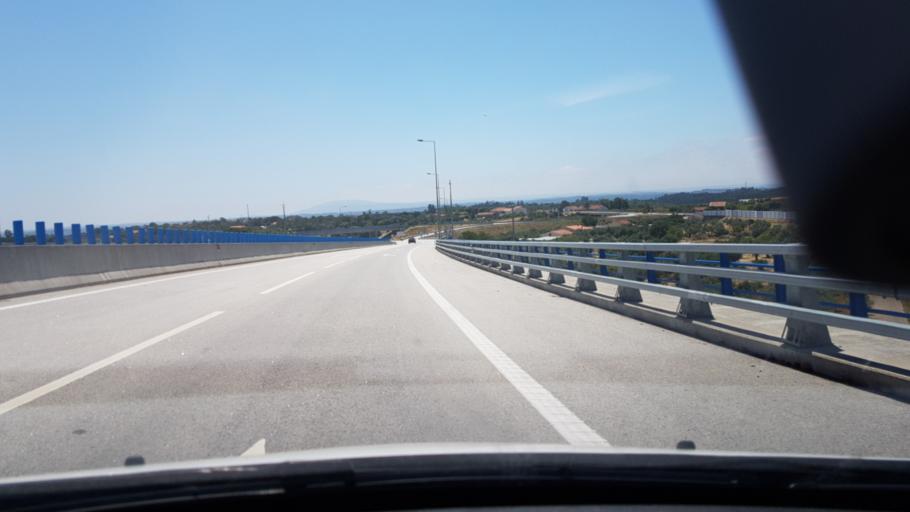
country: PT
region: Santarem
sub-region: Ferreira do Zezere
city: Ferreira do Zezere
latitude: 39.6700
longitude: -8.3535
